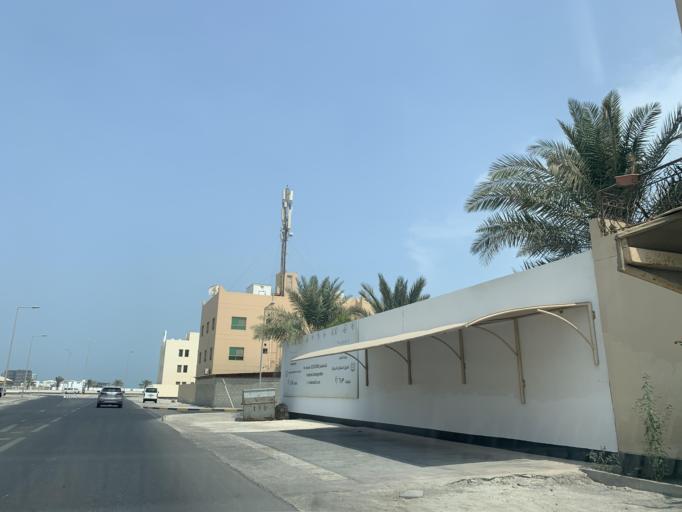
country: BH
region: Muharraq
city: Al Hadd
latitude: 26.2673
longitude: 50.6598
